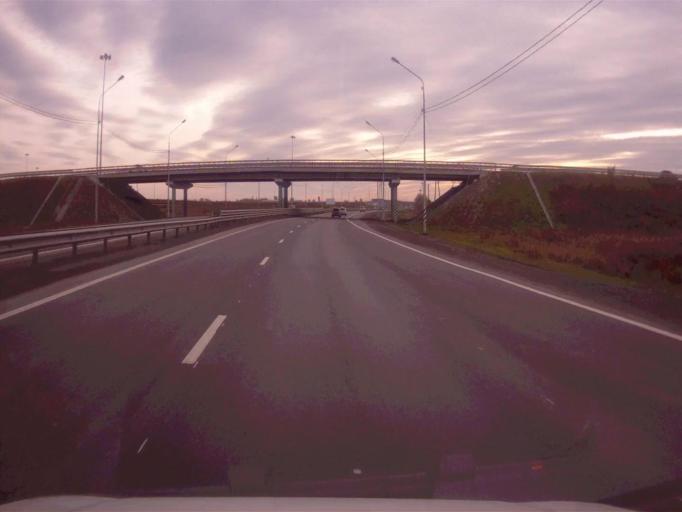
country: RU
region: Chelyabinsk
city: Novosineglazovskiy
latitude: 55.0028
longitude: 61.4539
